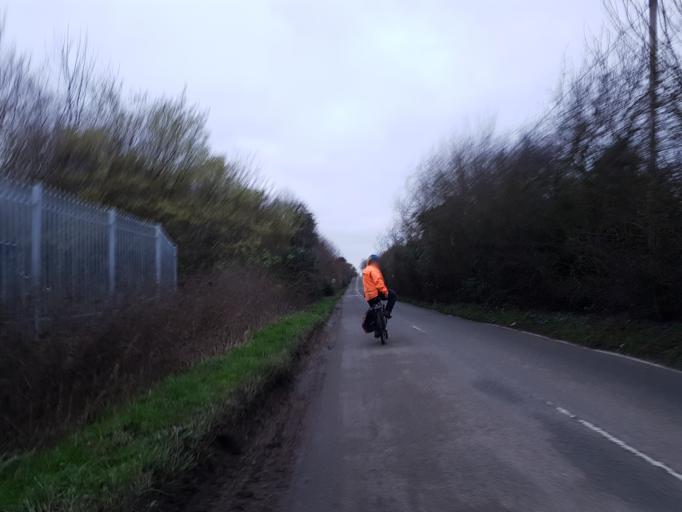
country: GB
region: England
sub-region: Cambridgeshire
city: Waterbeach
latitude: 52.2173
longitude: 0.1848
